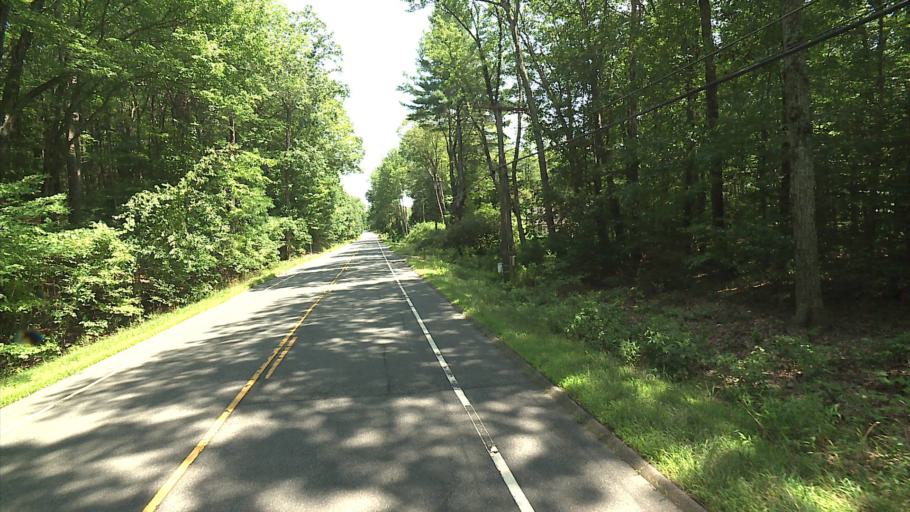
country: US
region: Connecticut
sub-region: Hartford County
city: North Granby
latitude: 41.9742
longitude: -72.8763
